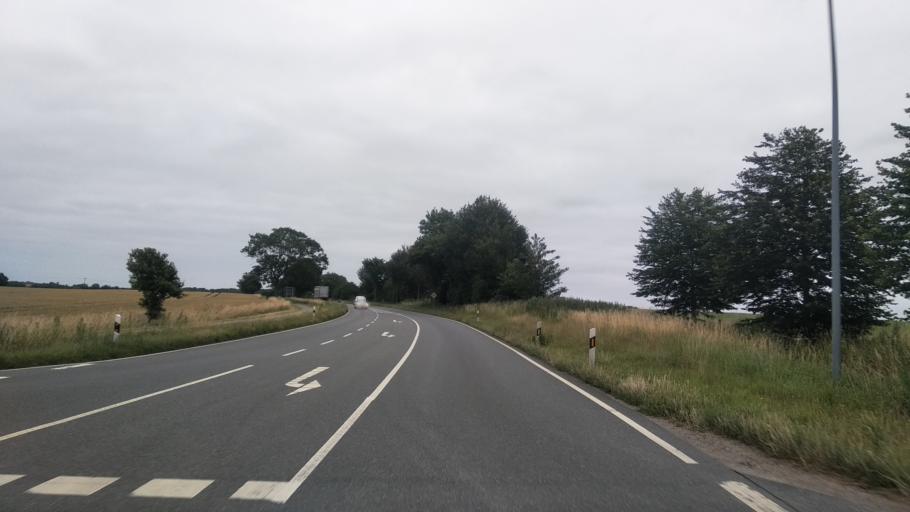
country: DE
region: Schleswig-Holstein
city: Ringsberg
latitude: 54.8034
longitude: 9.5982
